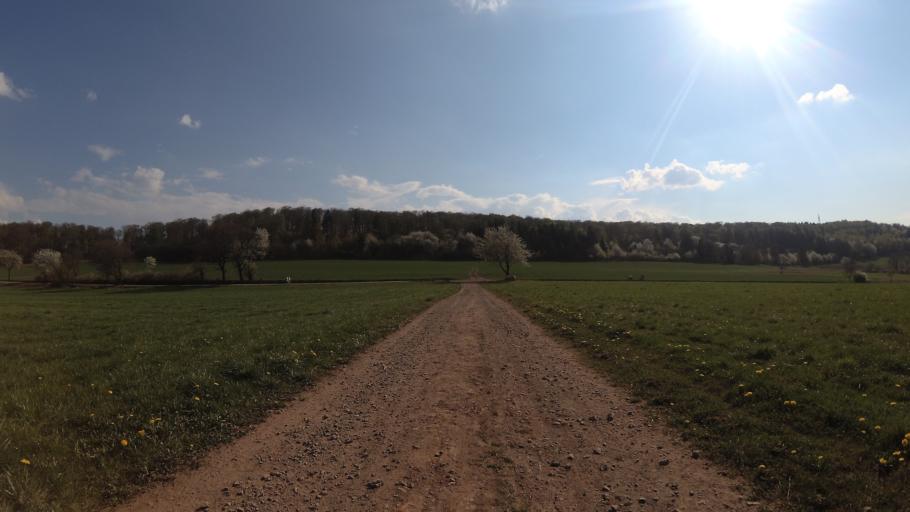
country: DE
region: Saarland
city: Sankt Wendel
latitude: 49.4444
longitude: 7.1791
